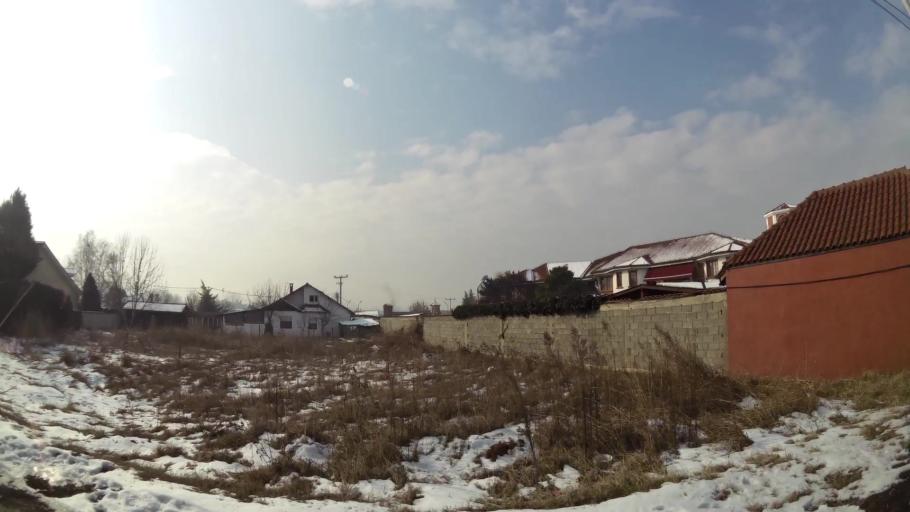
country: MK
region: Suto Orizari
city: Suto Orizare
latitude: 42.0168
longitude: 21.3863
